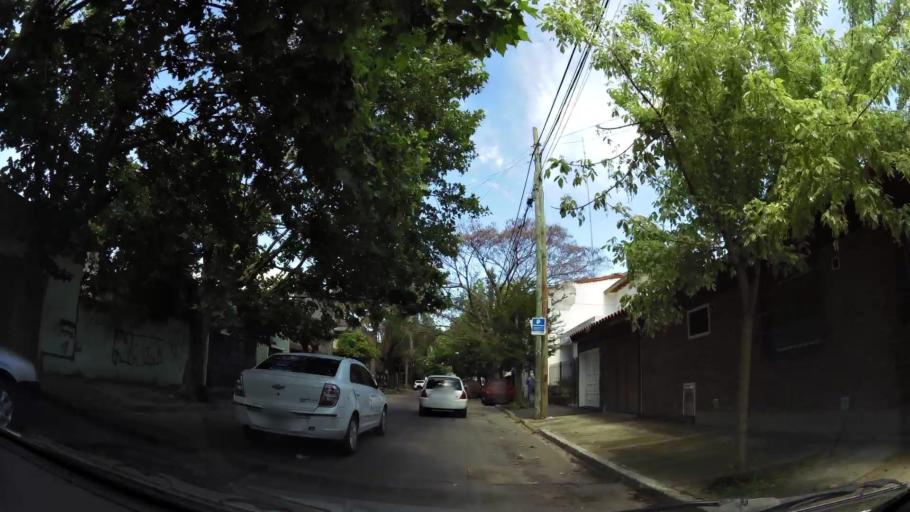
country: AR
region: Buenos Aires
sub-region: Partido de Quilmes
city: Quilmes
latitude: -34.7152
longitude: -58.2639
